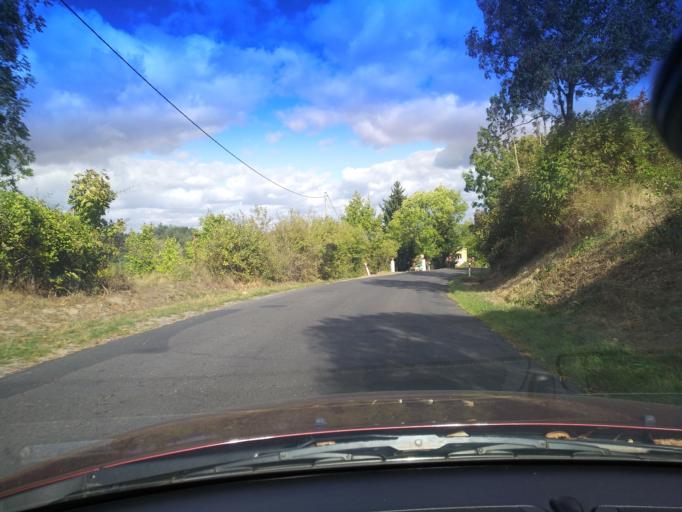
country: DE
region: Saxony
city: Goerlitz
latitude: 51.1618
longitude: 14.9978
